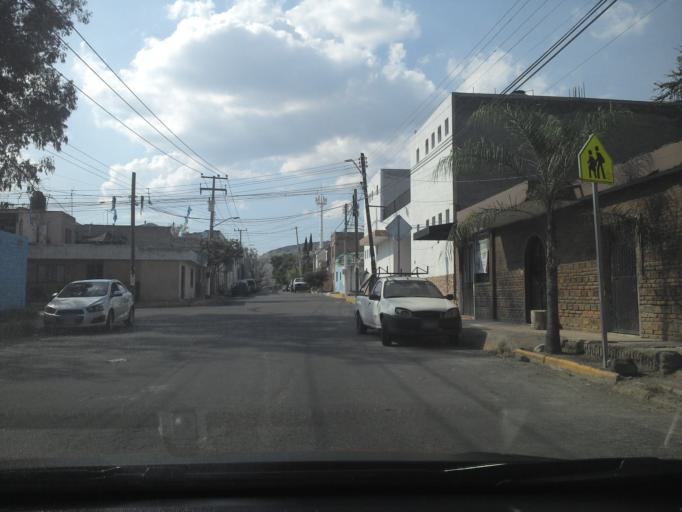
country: MX
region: Jalisco
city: Guadalajara
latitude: 20.6468
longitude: -103.4402
